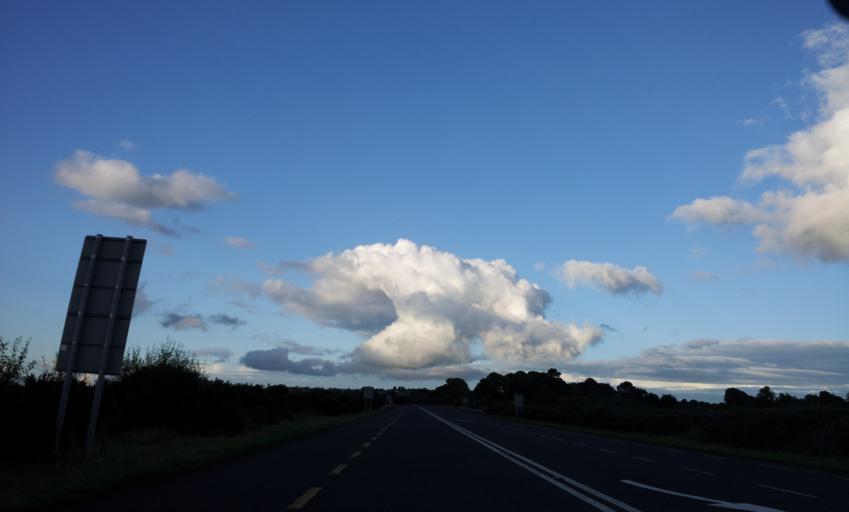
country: IE
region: Munster
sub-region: County Limerick
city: Abbeyfeale
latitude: 52.3462
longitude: -9.3382
